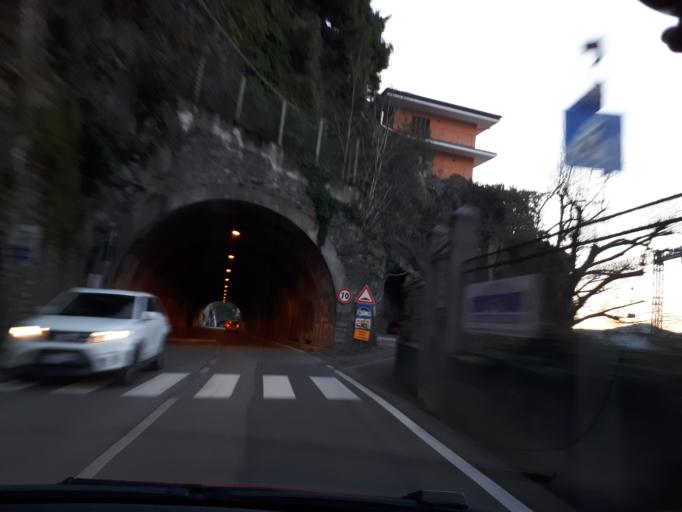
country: IT
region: Lombardy
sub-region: Provincia di Como
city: Blevio
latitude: 45.8345
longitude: 9.0970
